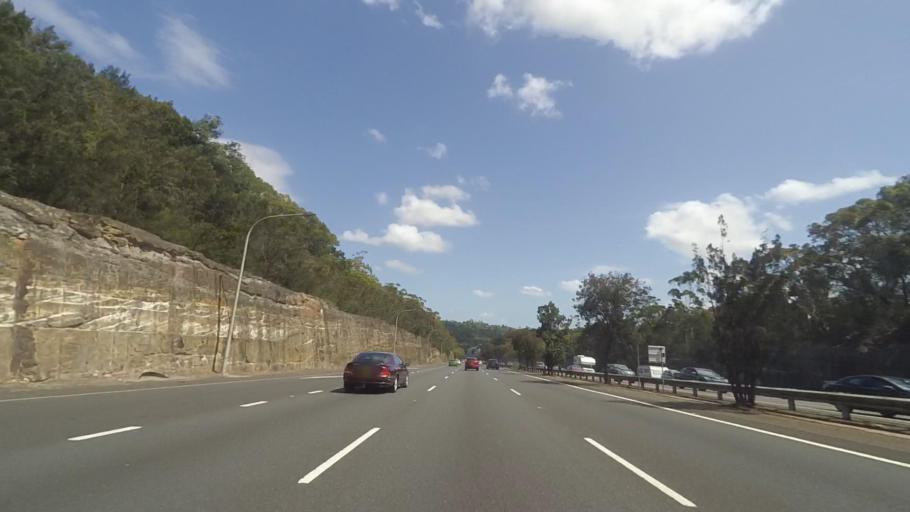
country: AU
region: New South Wales
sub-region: Hornsby Shire
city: Mount Colah
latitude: -33.6840
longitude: 151.1208
